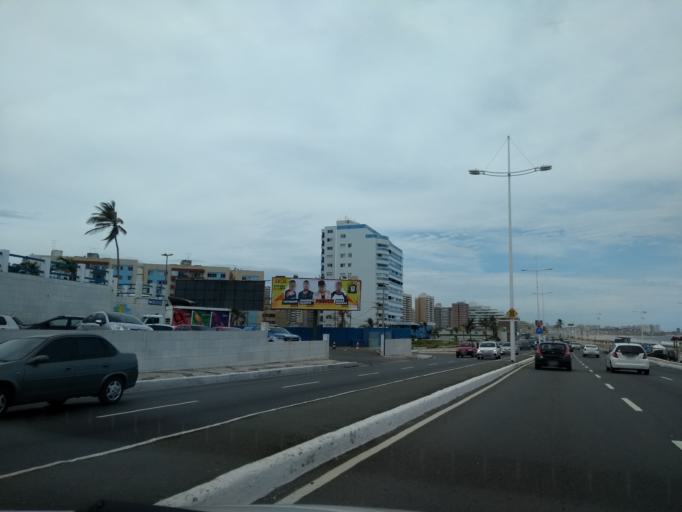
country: BR
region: Bahia
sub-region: Salvador
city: Salvador
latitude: -12.9950
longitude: -38.4414
